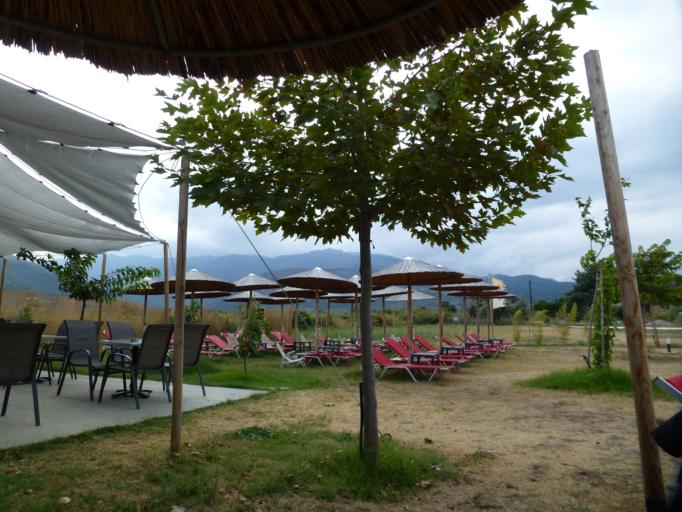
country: GR
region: East Macedonia and Thrace
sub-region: Nomos Kavalas
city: Prinos
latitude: 40.7511
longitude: 24.5622
